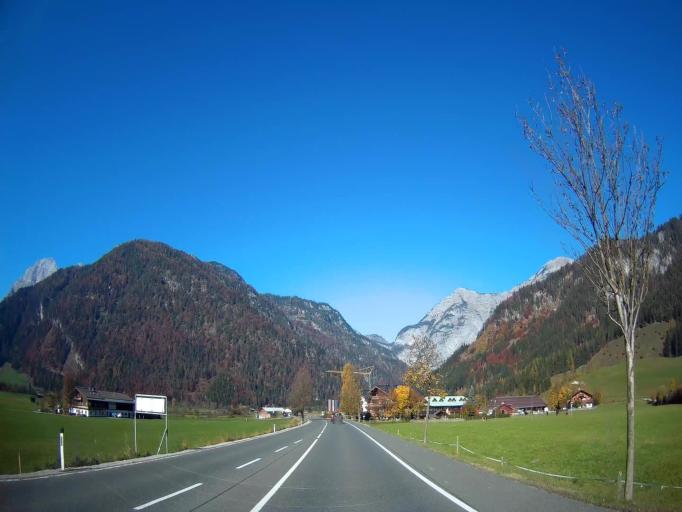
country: AT
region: Salzburg
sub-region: Politischer Bezirk Zell am See
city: Saalfelden am Steinernen Meer
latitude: 47.4525
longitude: 12.8330
